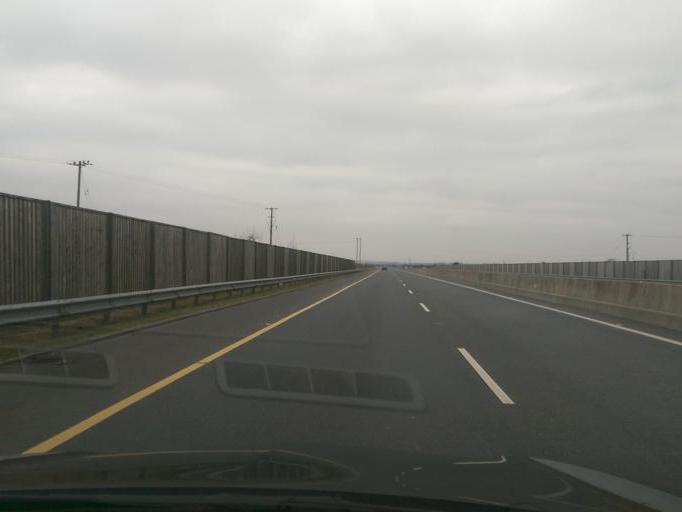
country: IE
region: Connaught
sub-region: County Galway
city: Oranmore
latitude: 53.2994
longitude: -8.8456
